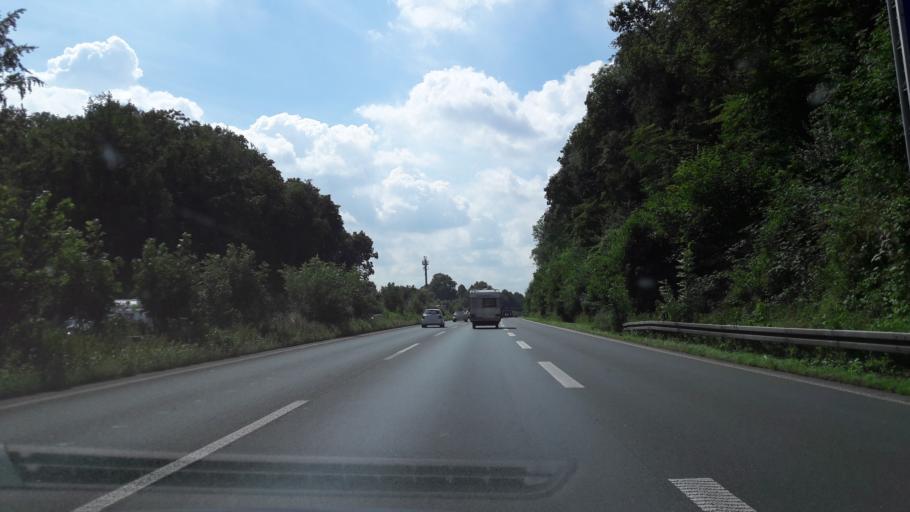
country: DE
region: North Rhine-Westphalia
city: Kamen
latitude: 51.6180
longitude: 7.6897
